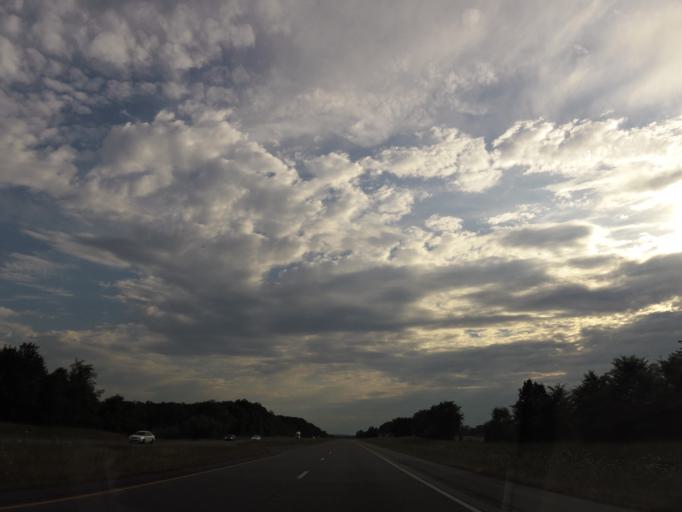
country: US
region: Alabama
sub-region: Lawrence County
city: Moulton
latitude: 34.5059
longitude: -87.2290
